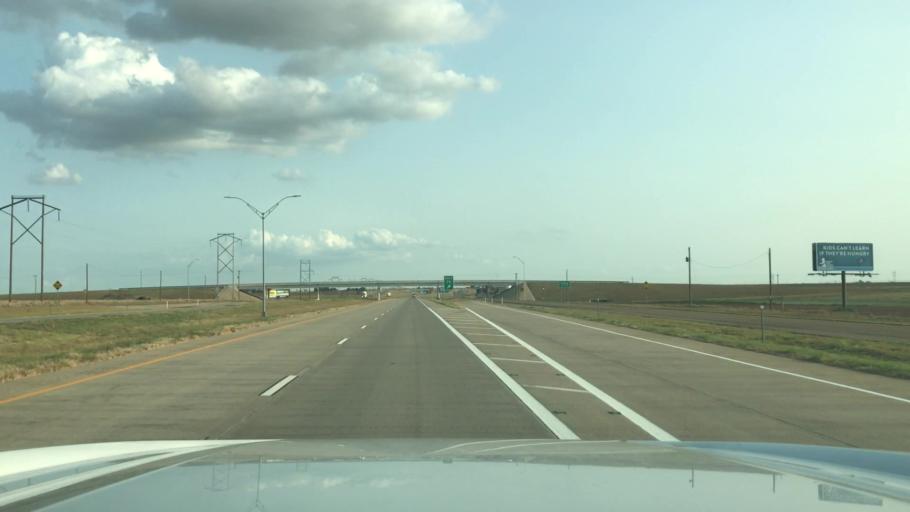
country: US
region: Texas
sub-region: Swisher County
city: Tulia
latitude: 34.5476
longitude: -101.7950
